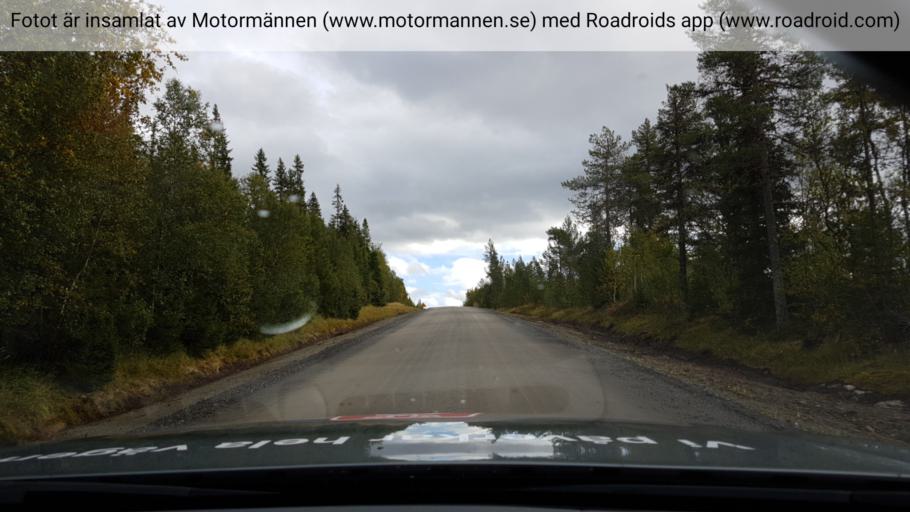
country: NO
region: Nord-Trondelag
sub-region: Snasa
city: Snaase
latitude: 63.7265
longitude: 12.5857
